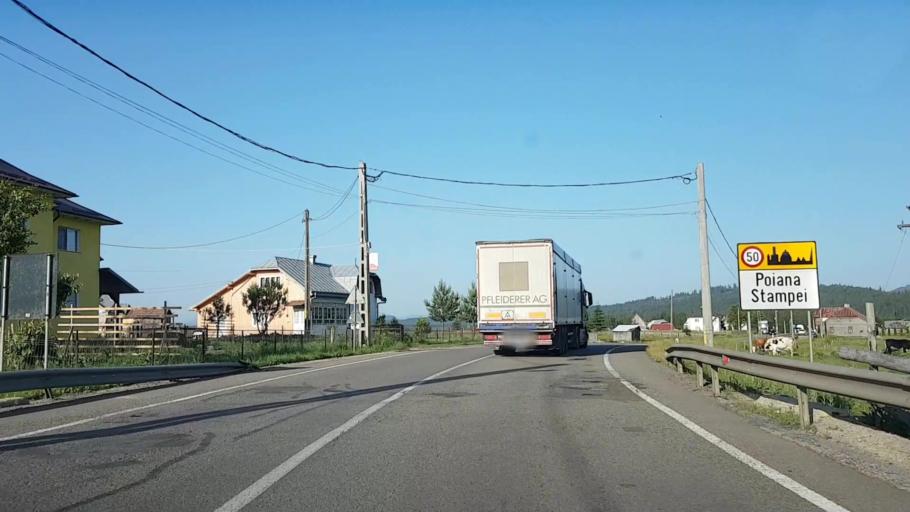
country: RO
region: Suceava
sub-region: Comuna Poiana Stampei
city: Poiana Stampei
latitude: 47.3005
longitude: 25.1008
